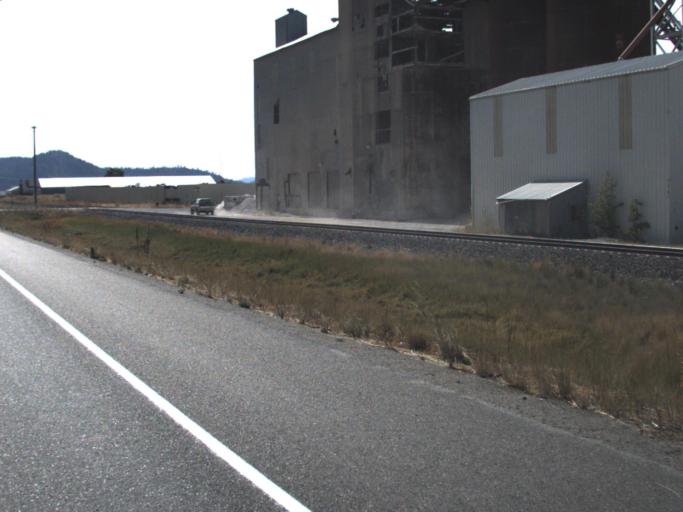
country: US
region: Washington
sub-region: Stevens County
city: Chewelah
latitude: 48.2528
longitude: -117.7153
